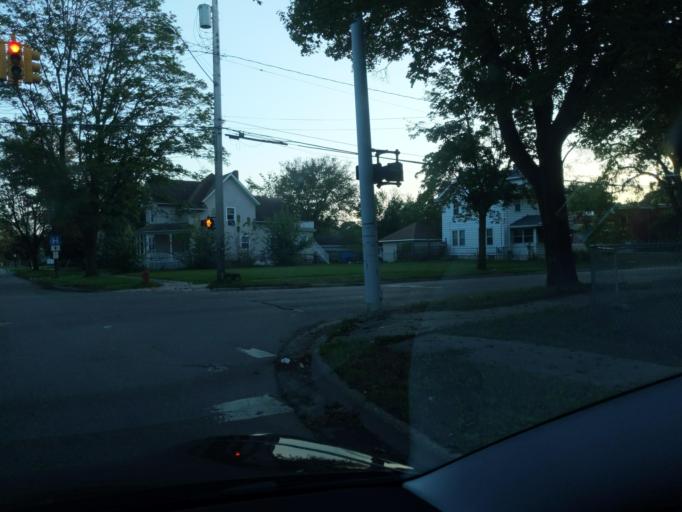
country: US
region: Michigan
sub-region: Jackson County
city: Jackson
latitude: 42.2549
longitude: -84.3845
